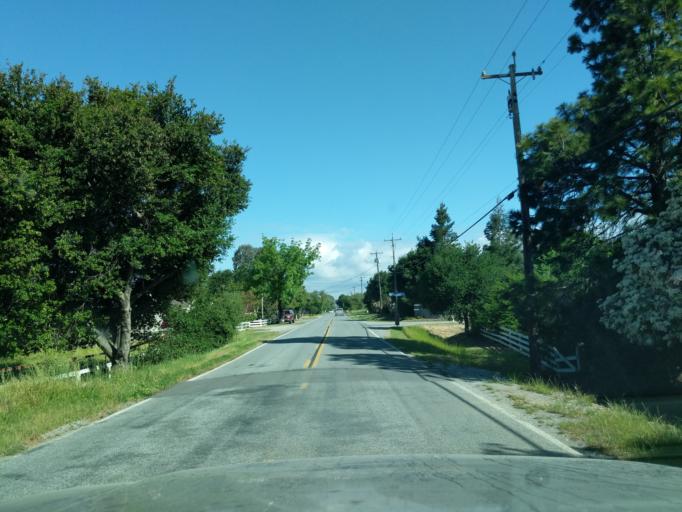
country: US
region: California
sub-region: Santa Clara County
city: San Martin
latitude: 37.0887
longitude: -121.5782
